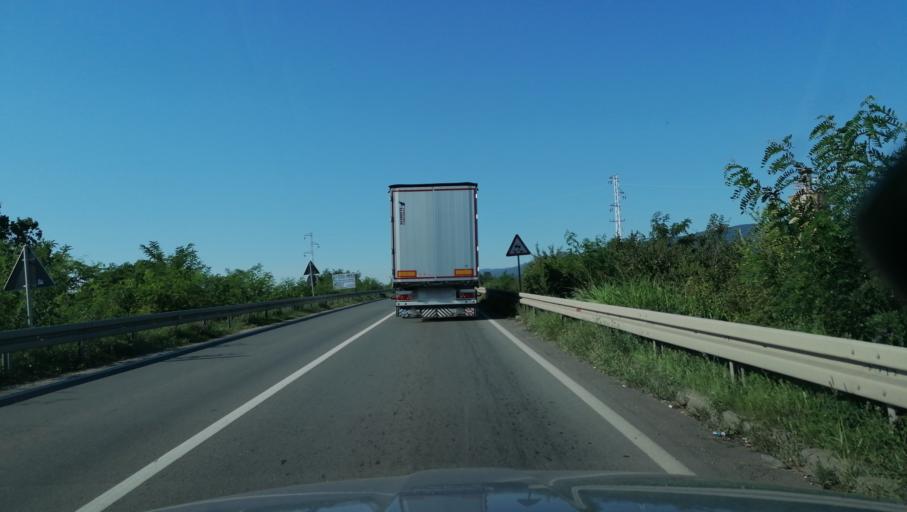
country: RS
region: Central Serbia
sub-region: Raski Okrug
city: Kraljevo
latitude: 43.7444
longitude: 20.6638
